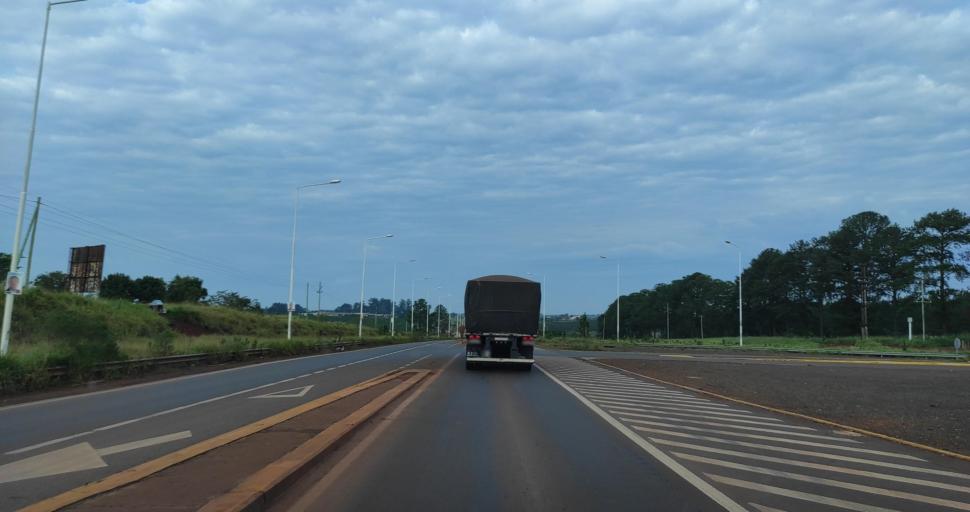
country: AR
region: Corrientes
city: Gobernador Ingeniero Valentin Virasoro
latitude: -27.9670
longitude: -56.0082
